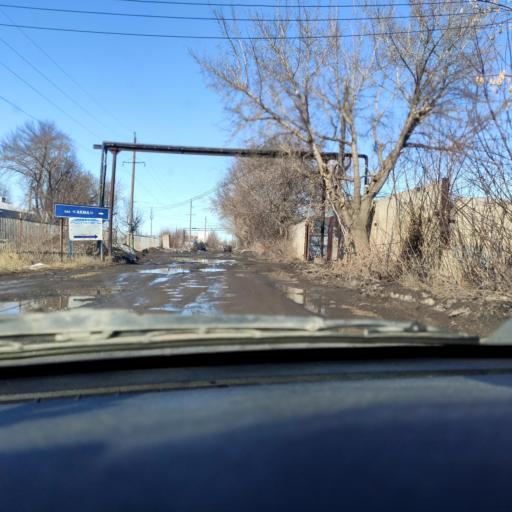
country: RU
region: Samara
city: Tol'yatti
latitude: 53.5884
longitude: 49.2581
